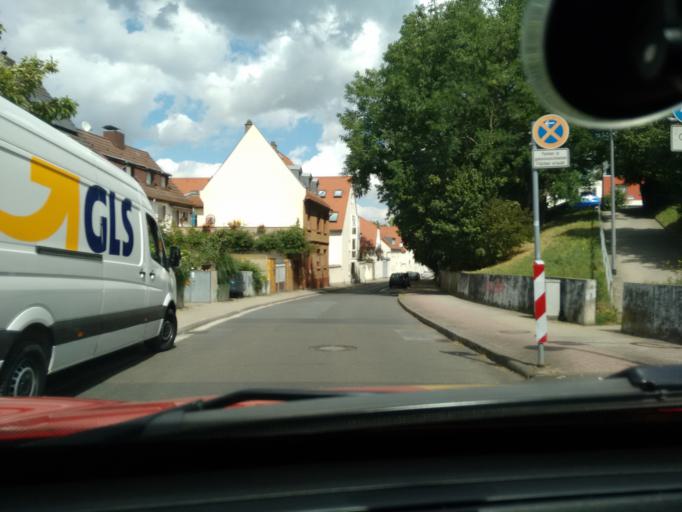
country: DE
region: Rheinland-Pfalz
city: Mainz
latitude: 49.9823
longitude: 8.2482
